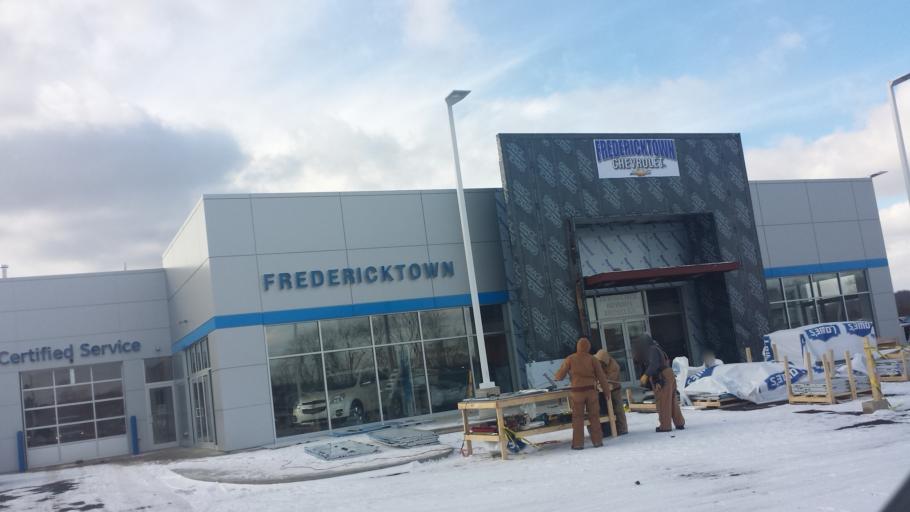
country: US
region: Ohio
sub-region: Knox County
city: Fredericktown
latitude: 40.4800
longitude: -82.5563
